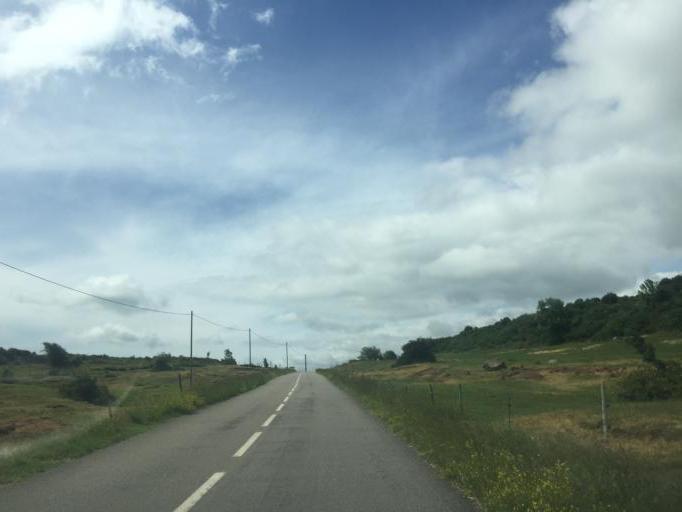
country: FR
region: Rhone-Alpes
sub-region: Departement de l'Ardeche
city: Saint-Priest
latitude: 44.6716
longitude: 4.5597
